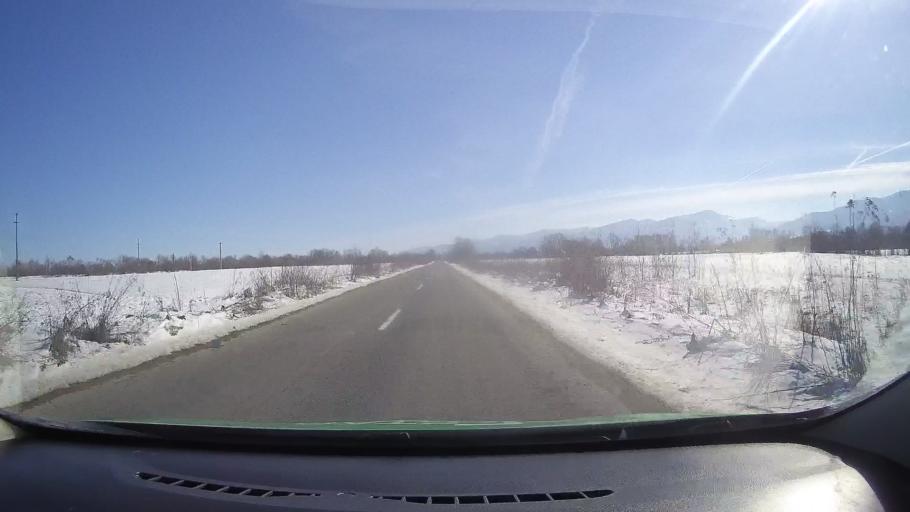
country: RO
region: Brasov
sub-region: Comuna Harseni
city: Harseni
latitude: 45.7330
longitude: 25.0168
